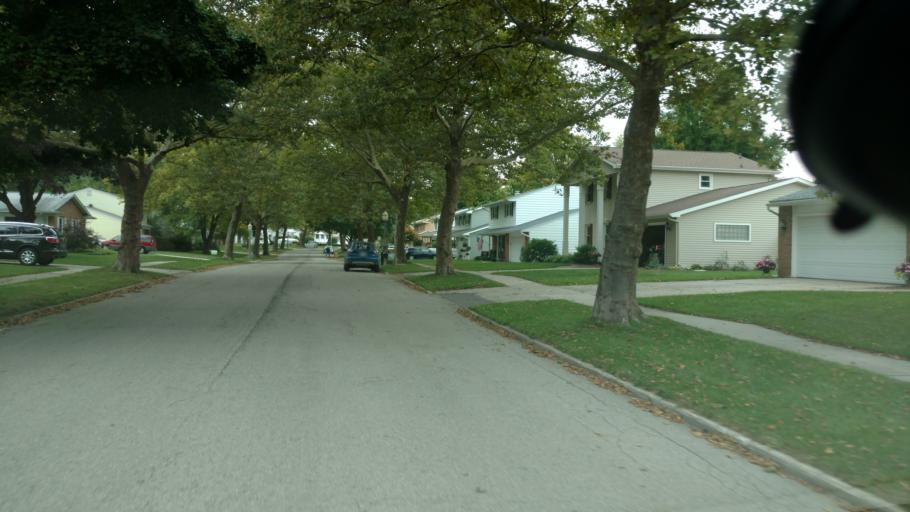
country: US
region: Michigan
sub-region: Ingham County
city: East Lansing
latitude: 42.7558
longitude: -84.5181
